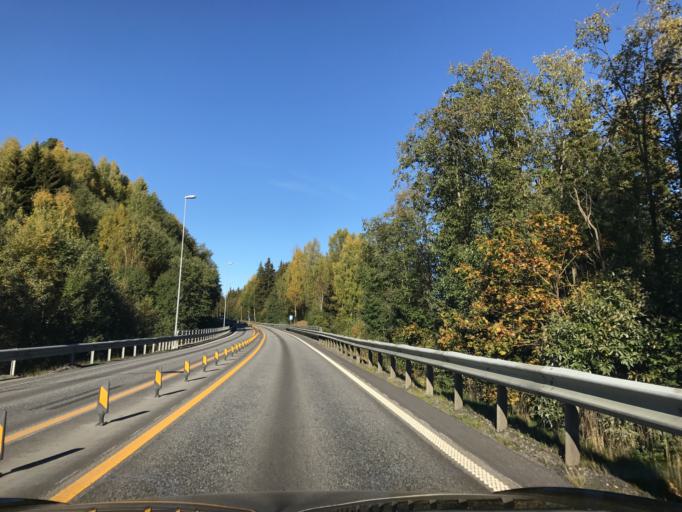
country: NO
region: Oppland
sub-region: Lillehammer
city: Lillehammer
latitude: 60.9999
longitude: 10.5003
